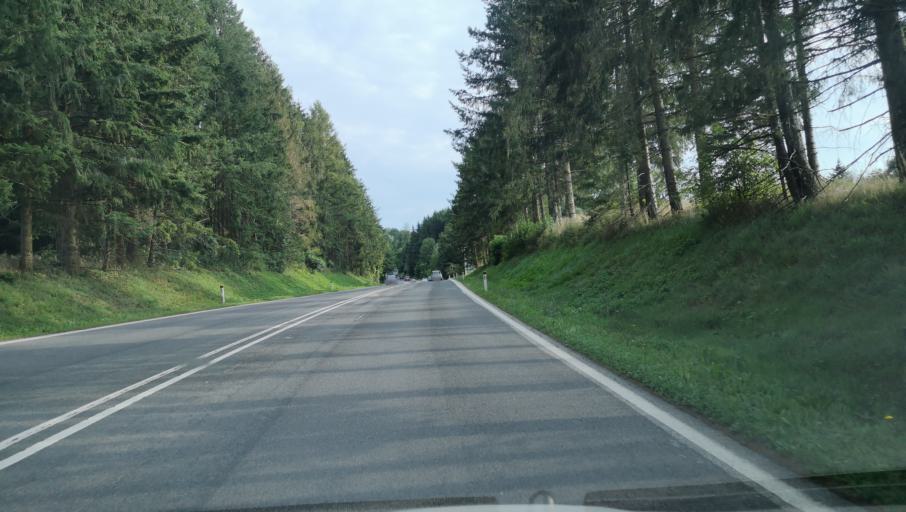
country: AT
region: Lower Austria
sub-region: Politischer Bezirk Amstetten
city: Amstetten
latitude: 48.1602
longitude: 14.8511
